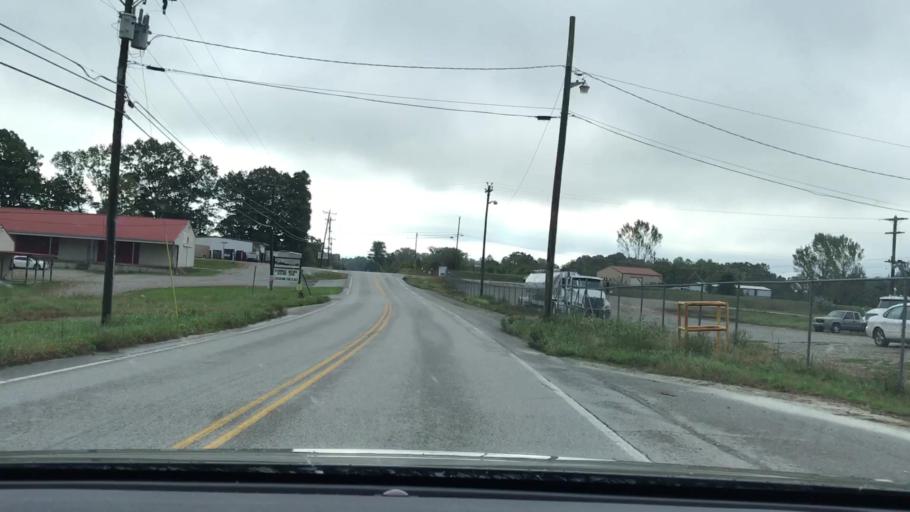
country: US
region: Tennessee
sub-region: Fentress County
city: Jamestown
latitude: 36.3873
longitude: -84.9345
